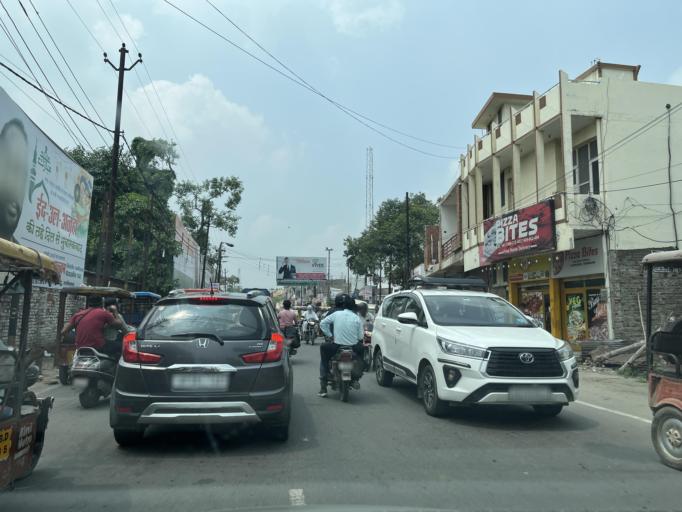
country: IN
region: Uttar Pradesh
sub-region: Bijnor
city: Najibabad
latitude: 29.6052
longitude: 78.3401
